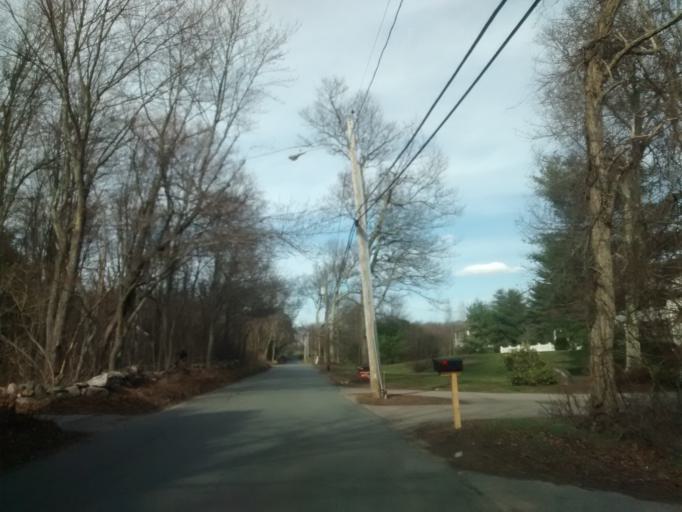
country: US
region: Massachusetts
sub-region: Norfolk County
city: Plainville
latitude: 42.0011
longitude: -71.3708
